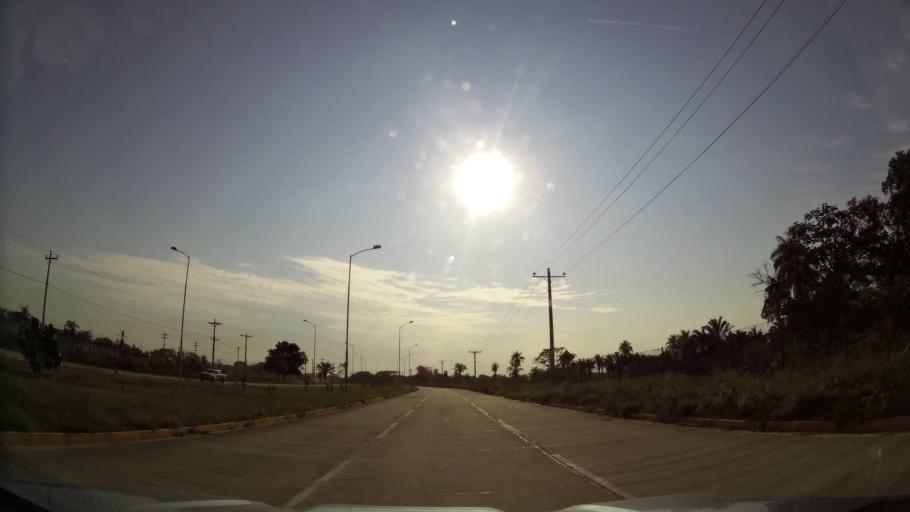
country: BO
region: Santa Cruz
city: Santa Cruz de la Sierra
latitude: -17.6919
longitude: -63.1164
